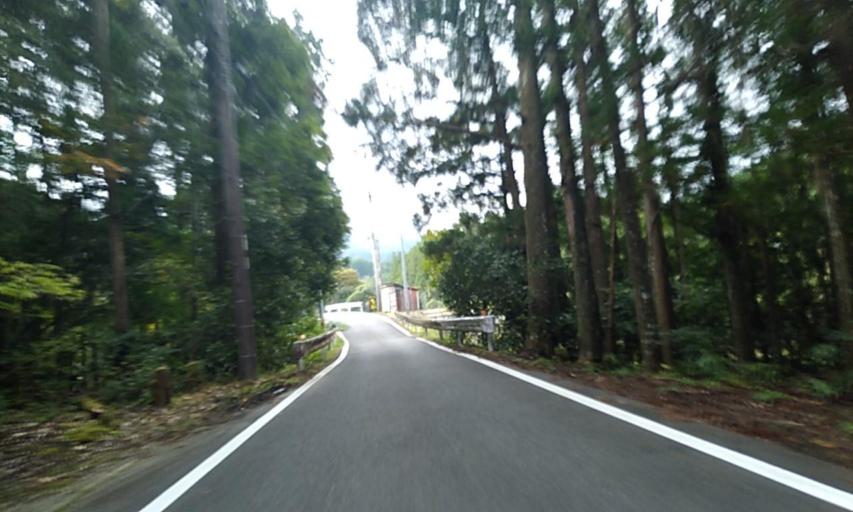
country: JP
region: Wakayama
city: Shingu
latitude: 33.9311
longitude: 135.9796
